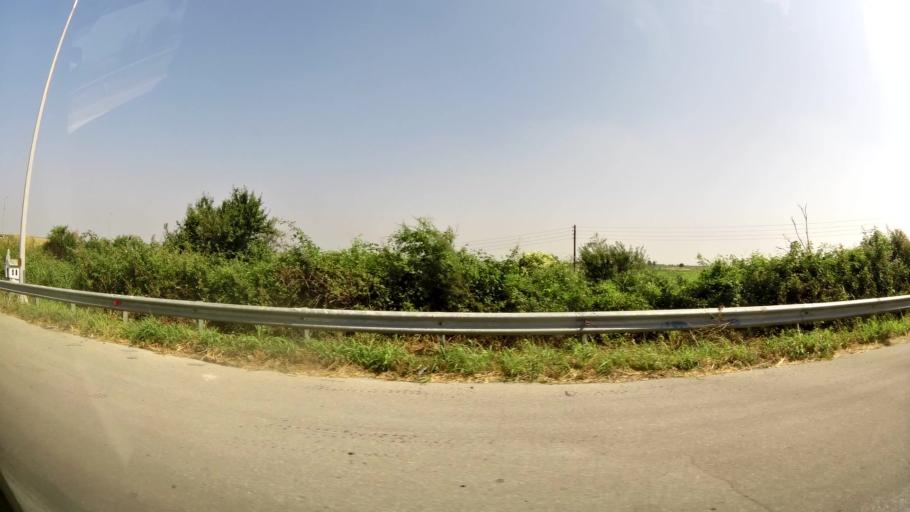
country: GR
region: Central Macedonia
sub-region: Nomos Imathias
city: Kleidi
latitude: 40.5568
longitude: 22.5962
